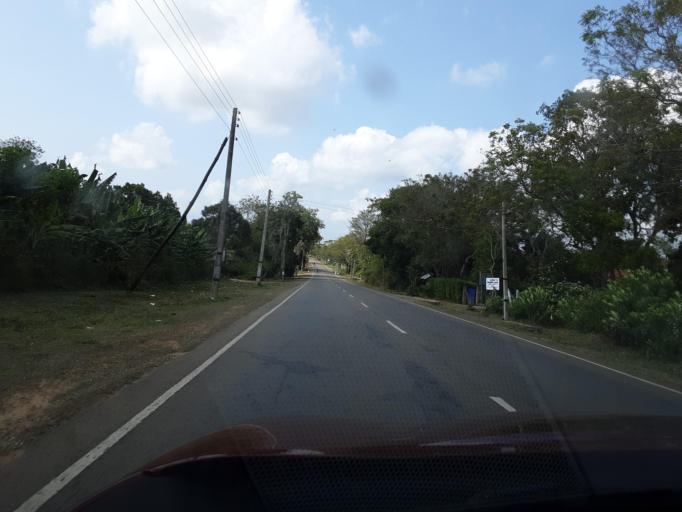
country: LK
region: Southern
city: Tangalla
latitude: 6.2746
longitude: 81.2286
